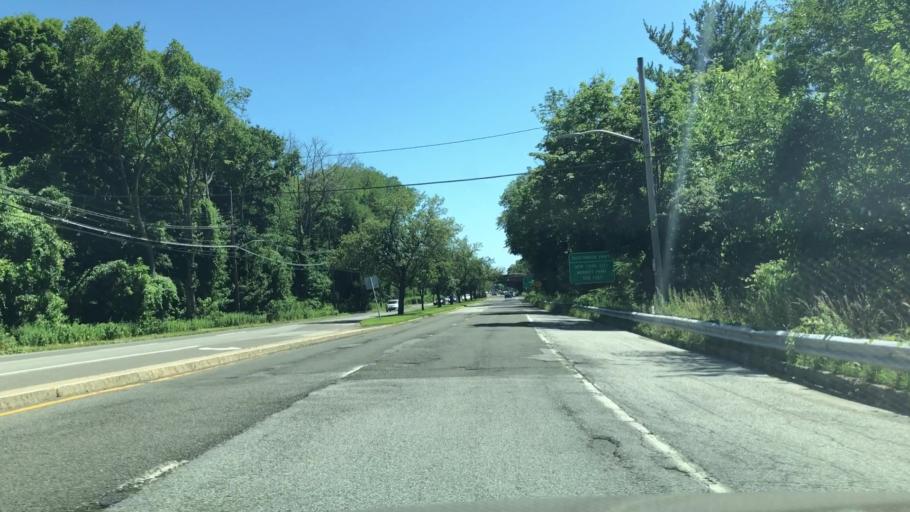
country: US
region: New York
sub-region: Westchester County
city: Harrison
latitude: 40.9863
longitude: -73.7448
